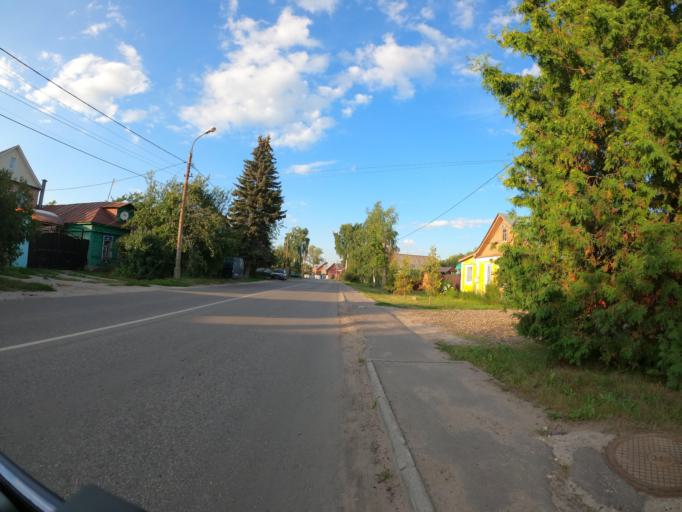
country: RU
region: Moskovskaya
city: Raduzhnyy
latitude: 55.1054
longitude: 38.7384
